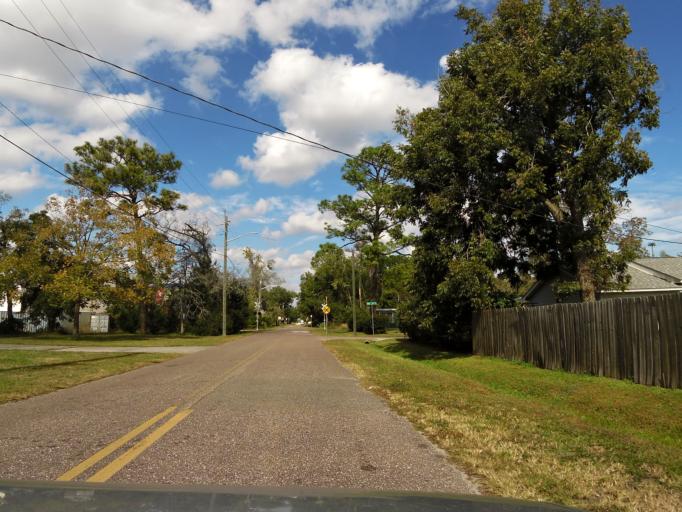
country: US
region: Florida
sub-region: Duval County
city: Jacksonville
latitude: 30.4075
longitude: -81.6461
